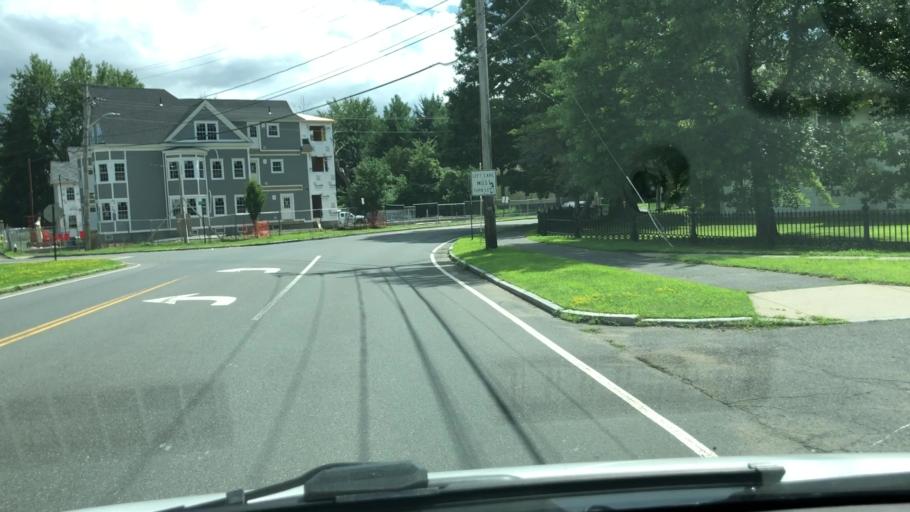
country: US
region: Massachusetts
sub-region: Hampshire County
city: Northampton
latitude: 42.3234
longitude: -72.6252
